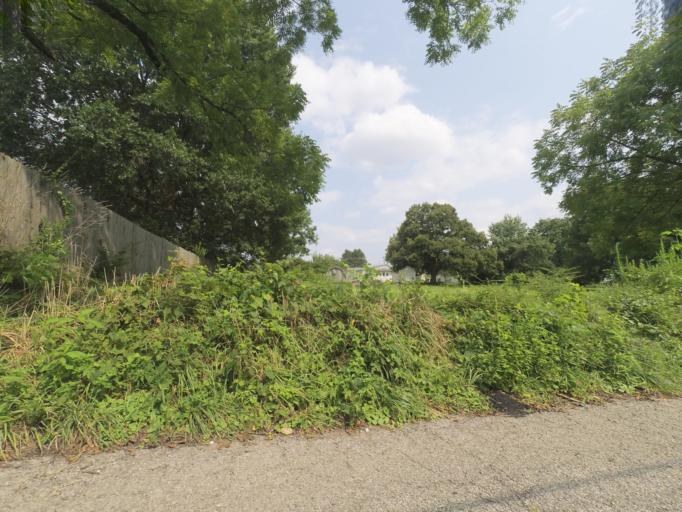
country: US
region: West Virginia
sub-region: Cabell County
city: Huntington
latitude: 38.4031
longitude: -82.4071
